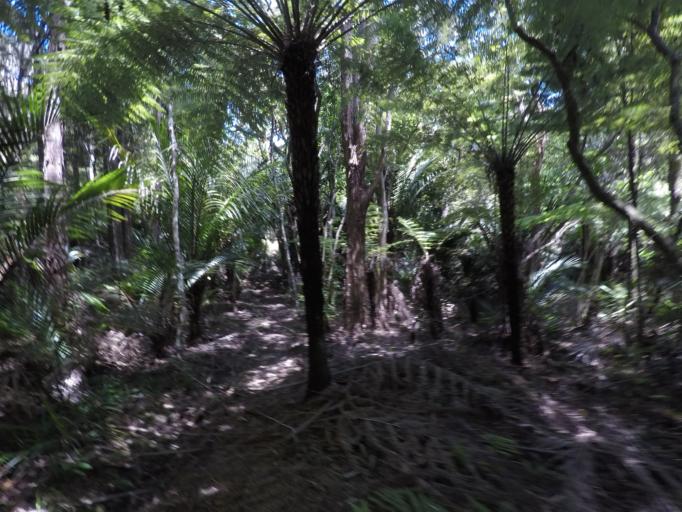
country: NZ
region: Auckland
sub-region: Auckland
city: Titirangi
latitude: -36.9713
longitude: 174.6321
